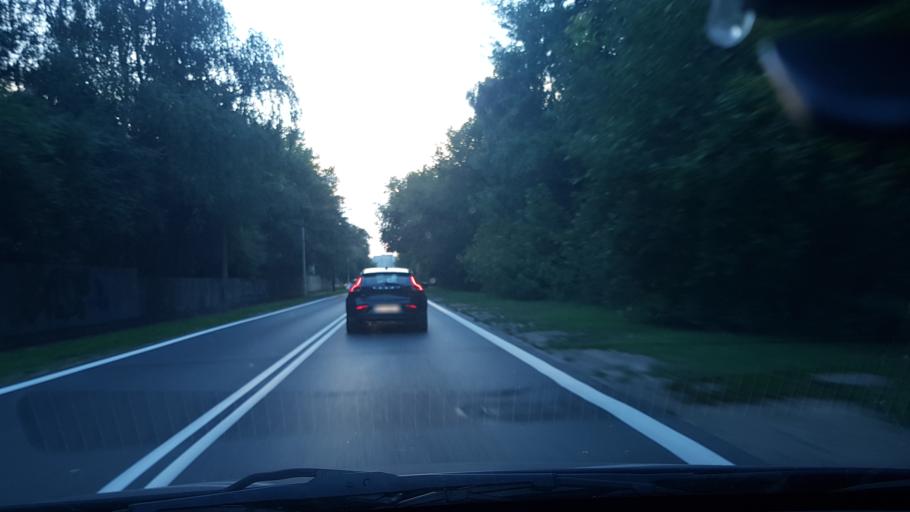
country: PL
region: Masovian Voivodeship
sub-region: Warszawa
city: Targowek
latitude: 52.2920
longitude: 21.0655
